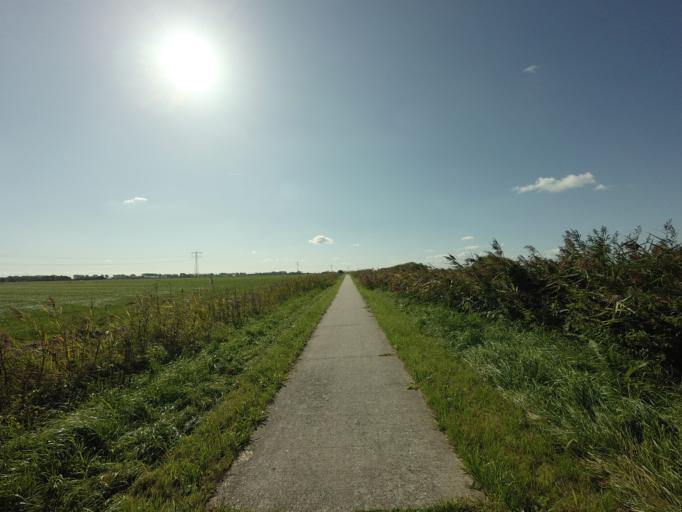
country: NL
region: Friesland
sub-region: Gemeente Boarnsterhim
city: Reduzum
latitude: 53.1468
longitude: 5.7639
